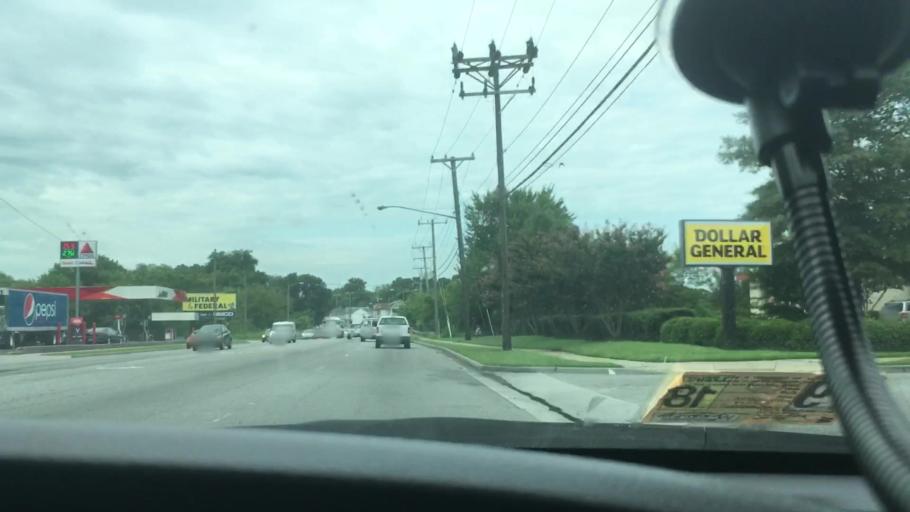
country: US
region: Virginia
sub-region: City of Norfolk
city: Norfolk
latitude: 36.8703
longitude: -76.2666
